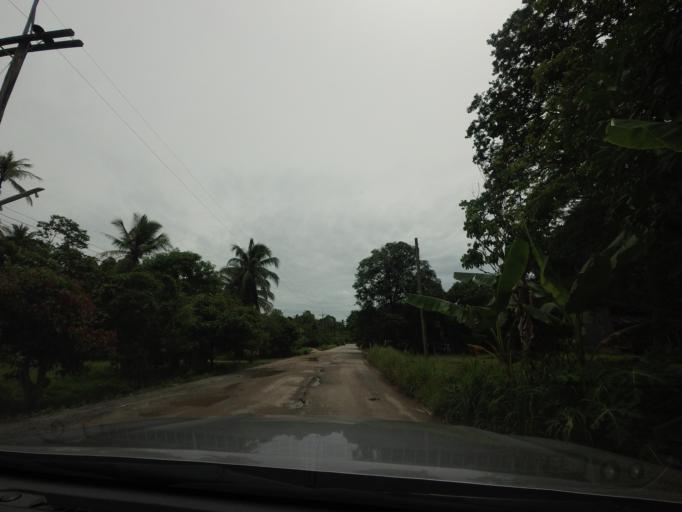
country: TH
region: Pattani
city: Sai Buri
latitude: 6.6535
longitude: 101.5537
